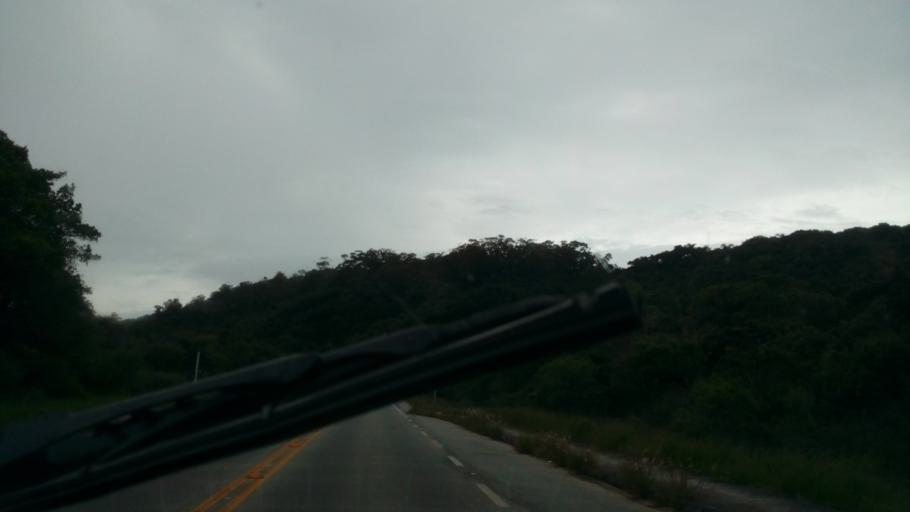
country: BR
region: Santa Catarina
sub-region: Laguna
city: Laguna
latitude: -28.5150
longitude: -48.7684
